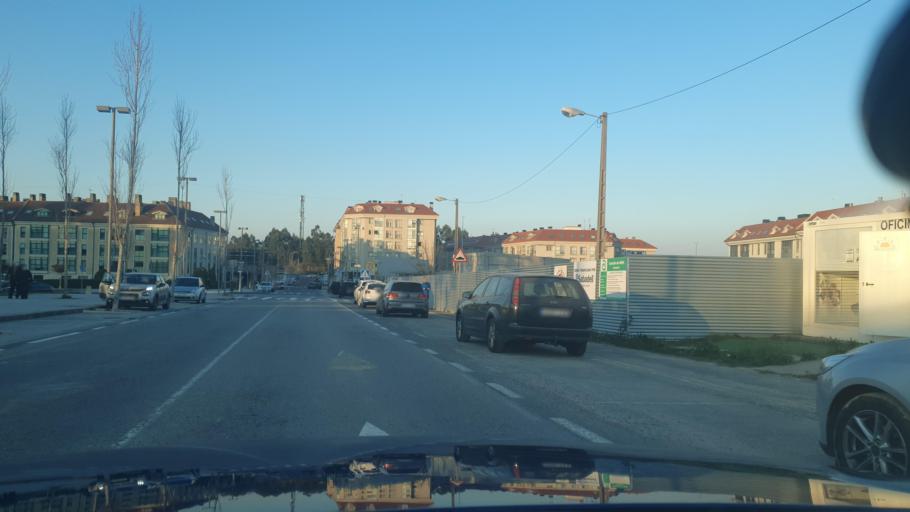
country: ES
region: Galicia
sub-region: Provincia da Coruna
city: Santiago de Compostela
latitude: 42.8458
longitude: -8.5805
